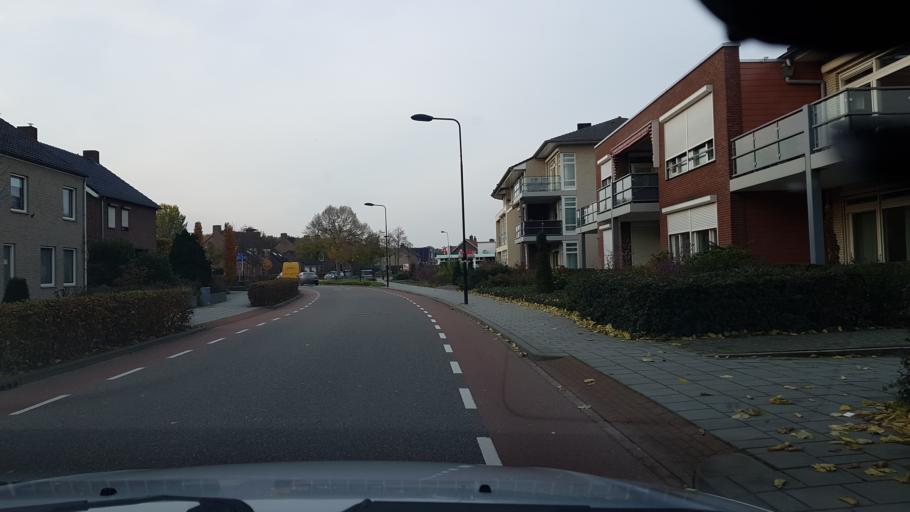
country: NL
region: Limburg
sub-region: Gemeente Beesel
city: Reuver
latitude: 51.2796
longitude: 6.0711
